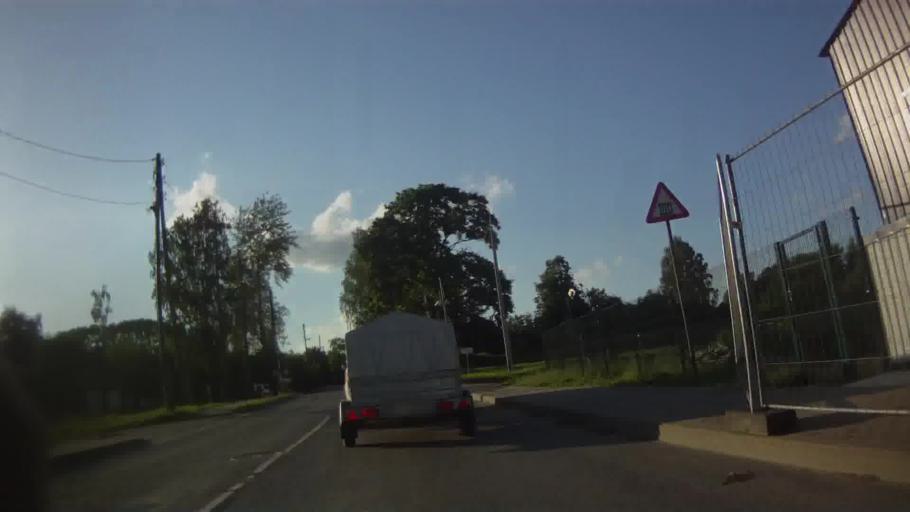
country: LV
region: Rezekne
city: Rezekne
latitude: 56.5139
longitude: 27.3238
